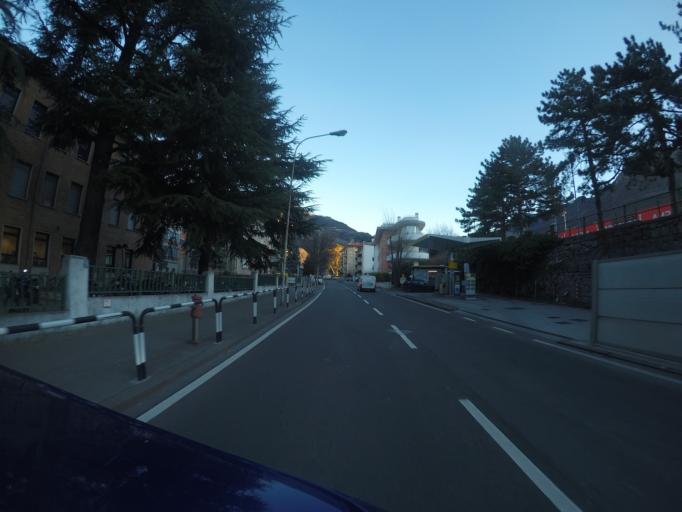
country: IT
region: Trentino-Alto Adige
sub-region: Bolzano
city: Bolzano
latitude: 46.5054
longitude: 11.3469
